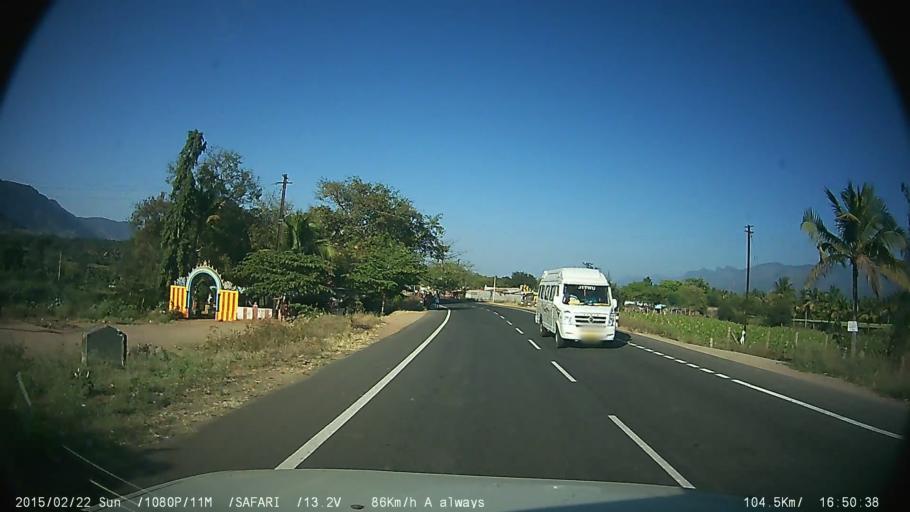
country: IN
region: Tamil Nadu
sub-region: Theni
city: Gudalur
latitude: 9.6432
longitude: 77.2116
